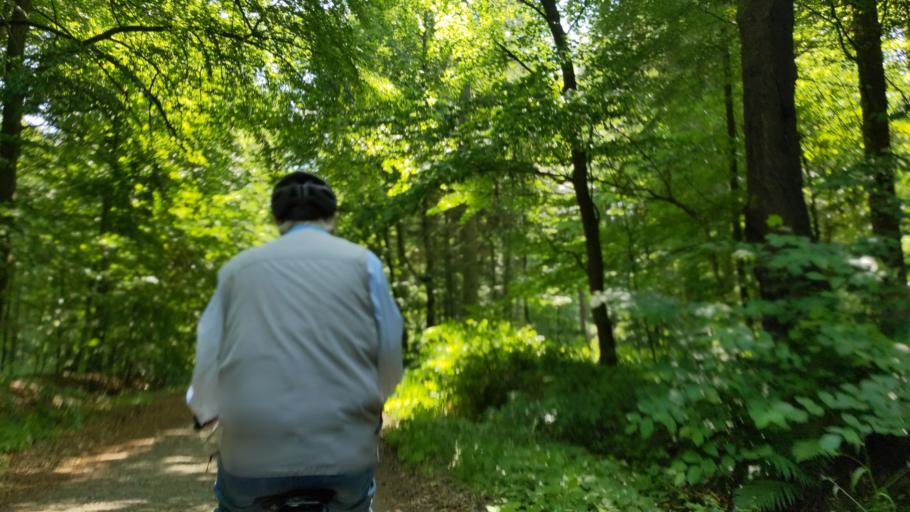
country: DE
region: Schleswig-Holstein
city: Albsfelde
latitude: 53.6915
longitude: 10.6847
